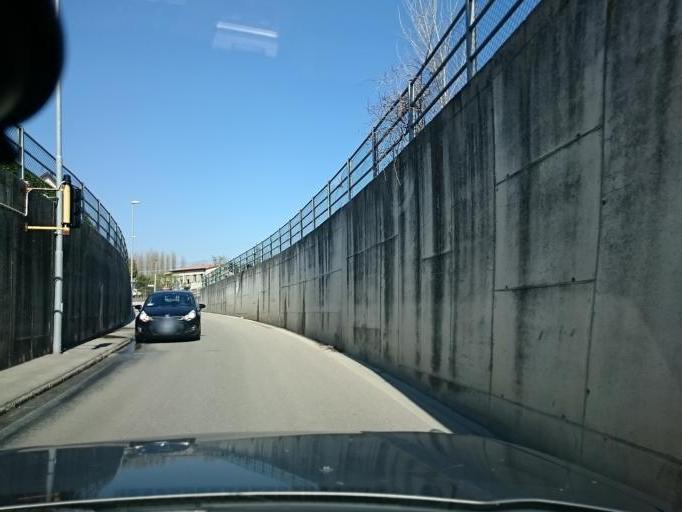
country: IT
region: Veneto
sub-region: Provincia di Padova
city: Albignasego
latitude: 45.3695
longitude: 11.8950
